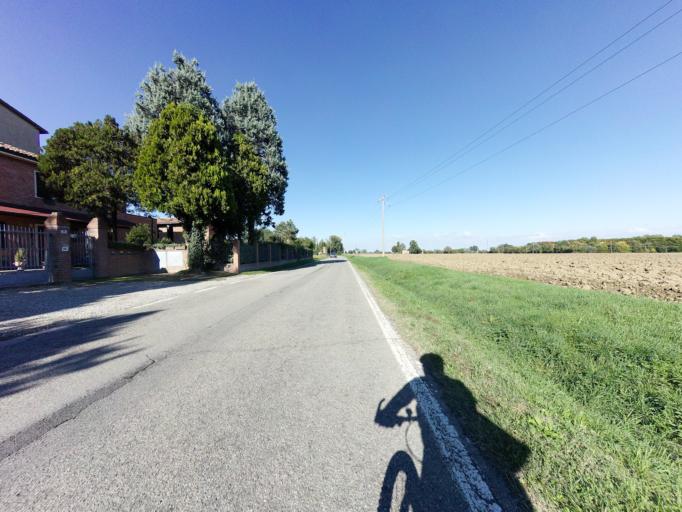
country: IT
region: Emilia-Romagna
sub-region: Provincia di Bologna
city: Progresso
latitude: 44.5618
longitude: 11.3908
